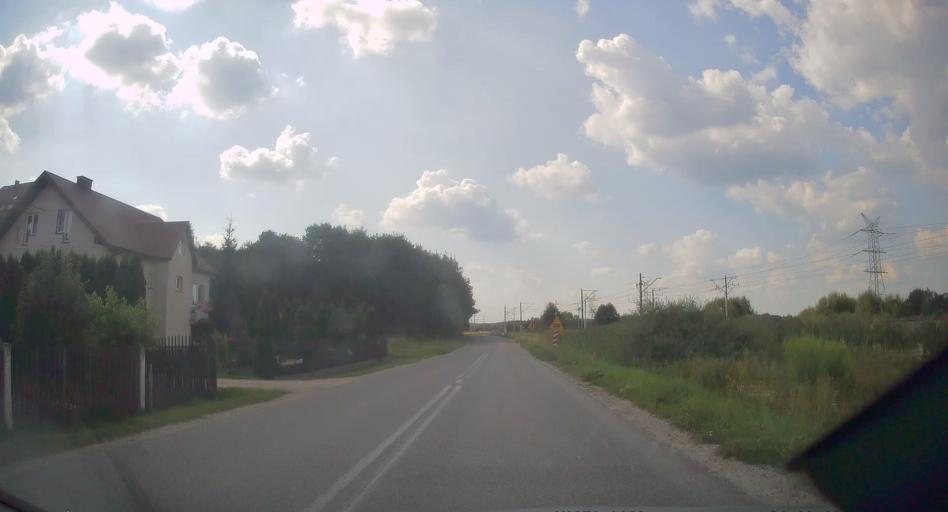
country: PL
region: Swietokrzyskie
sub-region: Powiat jedrzejowski
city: Malogoszcz
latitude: 50.8651
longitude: 20.3257
